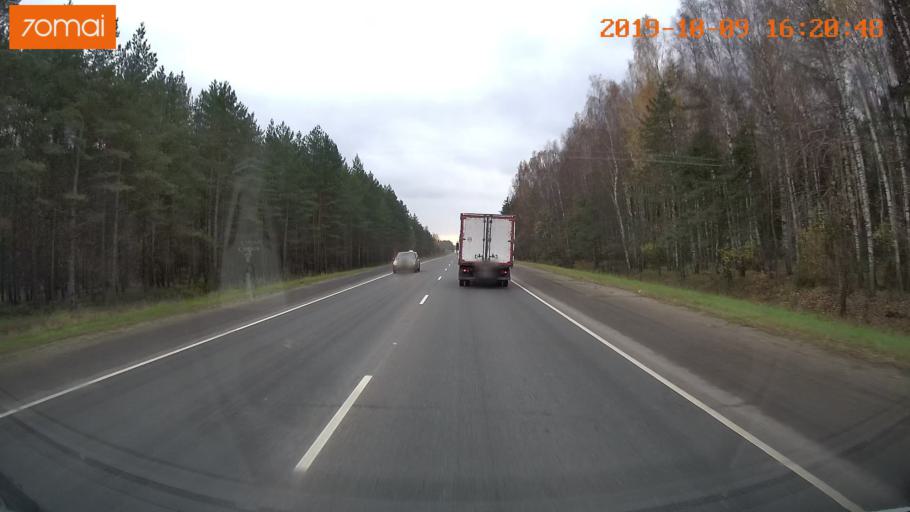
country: RU
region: Kostroma
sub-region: Kostromskoy Rayon
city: Kostroma
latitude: 57.7018
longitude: 40.8912
